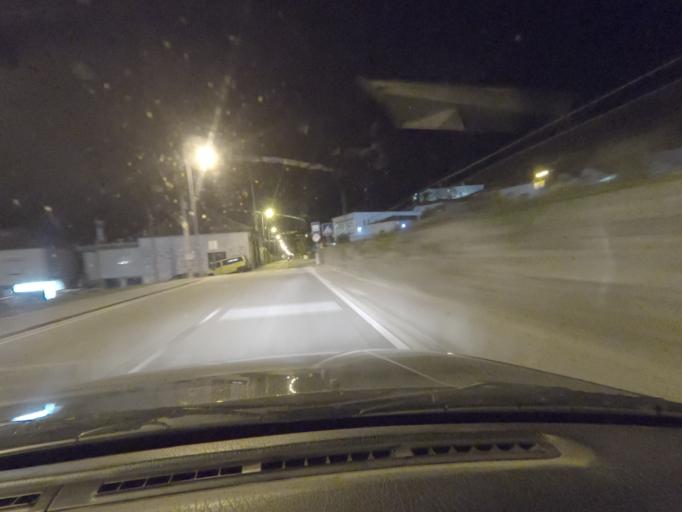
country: PT
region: Vila Real
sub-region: Peso da Regua
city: Godim
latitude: 41.1778
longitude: -7.7954
